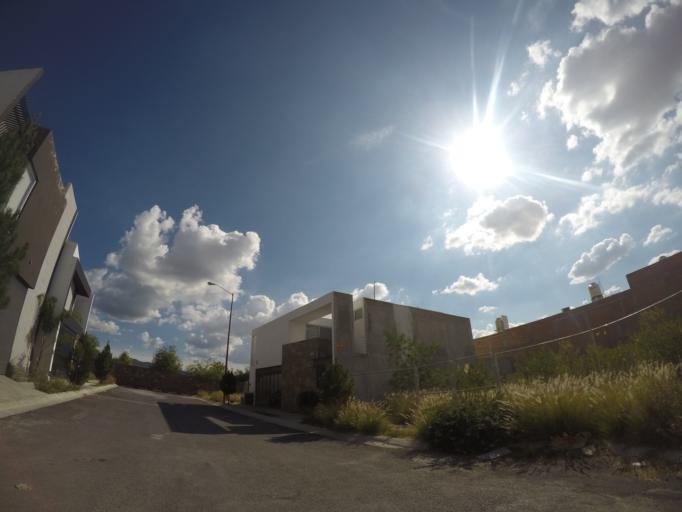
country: MX
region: San Luis Potosi
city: Escalerillas
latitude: 22.1215
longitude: -101.0333
